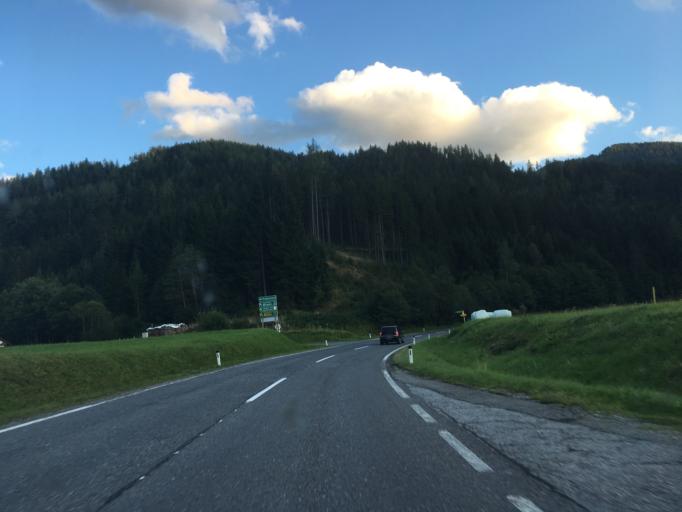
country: AT
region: Styria
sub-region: Politischer Bezirk Murtal
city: Hohentauern
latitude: 47.4466
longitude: 14.5099
